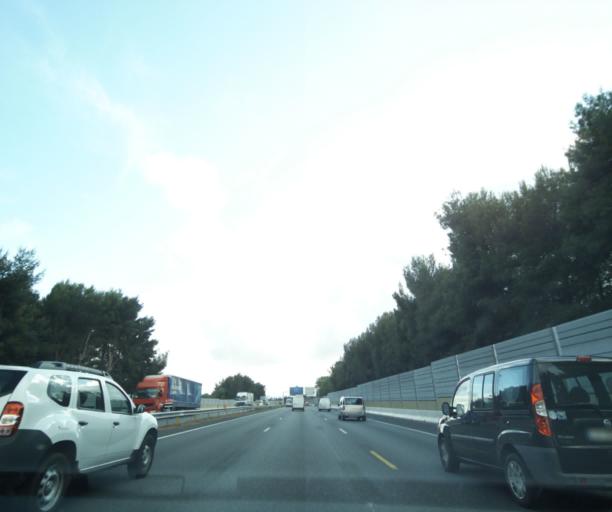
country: FR
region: Languedoc-Roussillon
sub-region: Departement de l'Herault
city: Lattes
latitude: 43.5914
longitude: 3.9005
